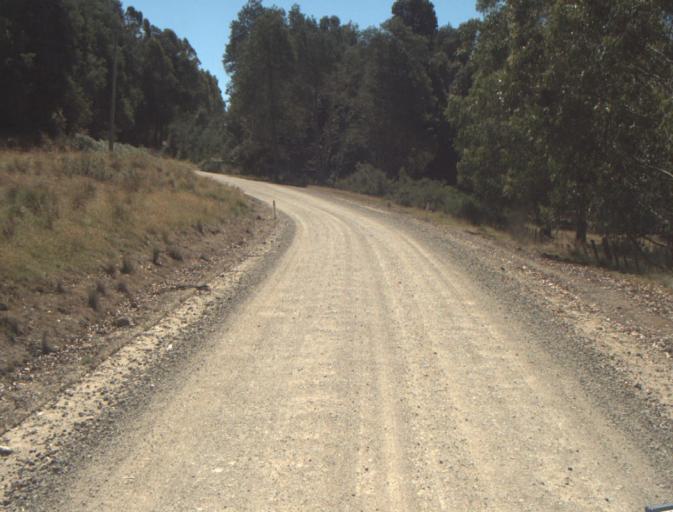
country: AU
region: Tasmania
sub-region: Dorset
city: Scottsdale
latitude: -41.3654
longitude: 147.4670
